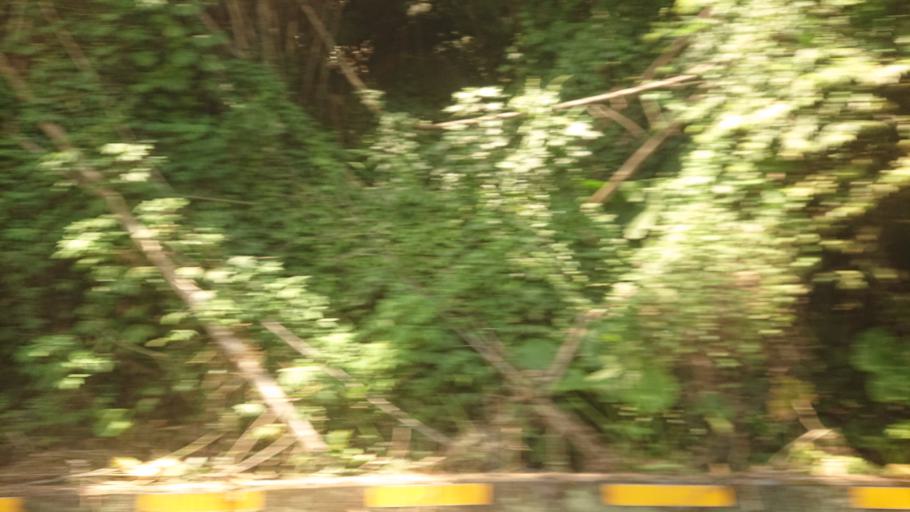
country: TW
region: Taiwan
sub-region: Nantou
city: Puli
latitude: 24.0626
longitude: 120.9462
